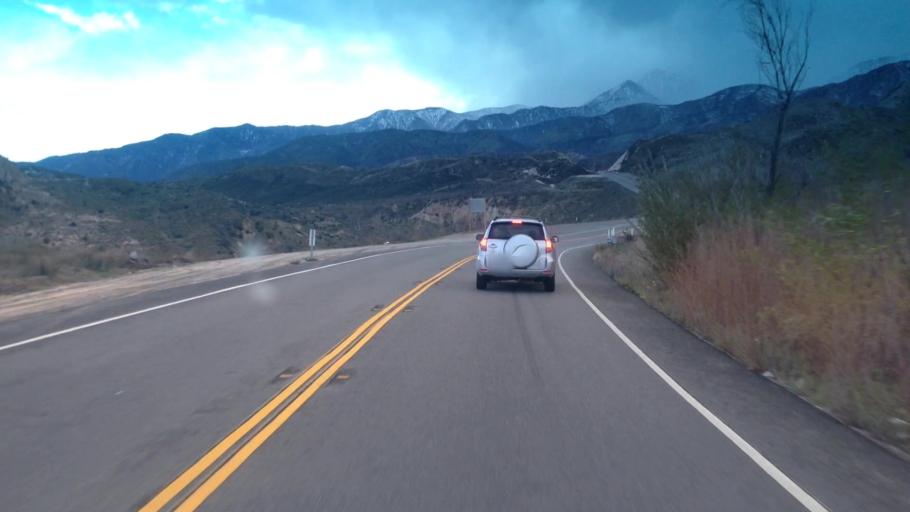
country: US
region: California
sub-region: San Bernardino County
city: Oak Hills
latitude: 34.3216
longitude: -117.4596
